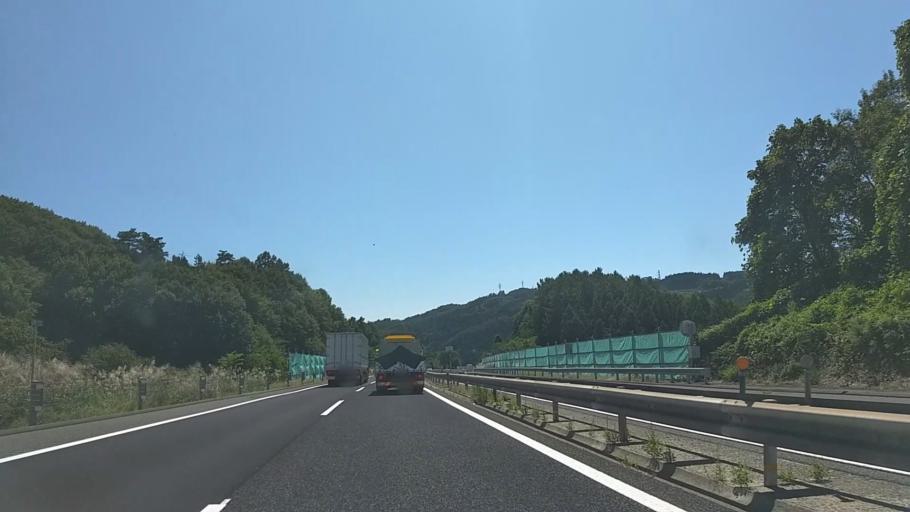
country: JP
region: Nagano
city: Nakano
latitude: 36.7901
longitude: 138.3216
